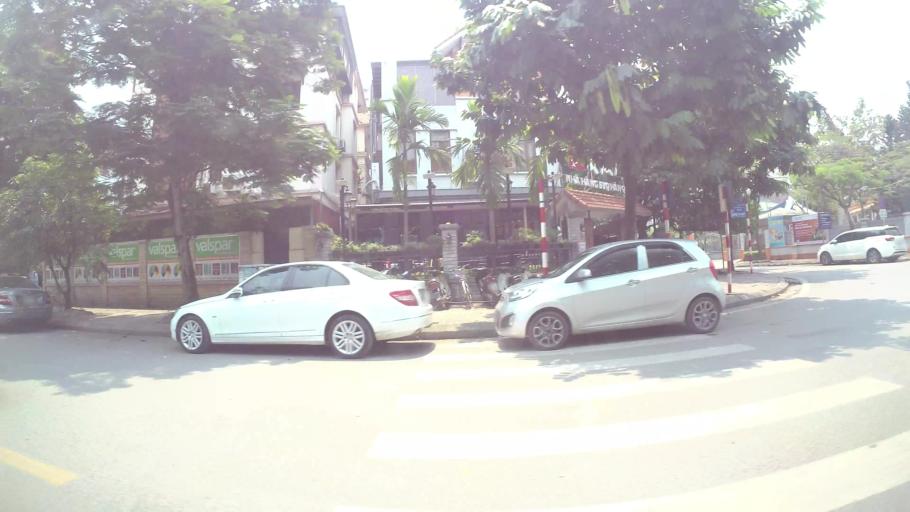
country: VN
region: Ha Noi
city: Thanh Xuan
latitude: 21.0083
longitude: 105.8048
